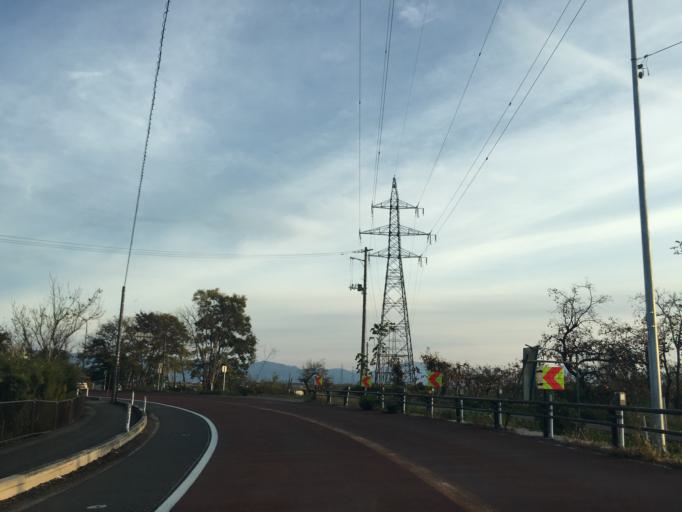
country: JP
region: Fukushima
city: Kitakata
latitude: 37.5540
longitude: 139.8630
